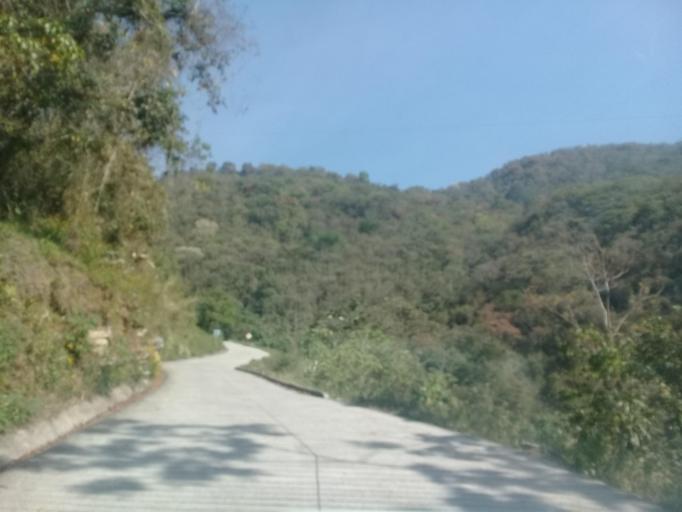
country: MX
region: Veracruz
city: Rafael Delgado
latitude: 18.7821
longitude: -97.0250
